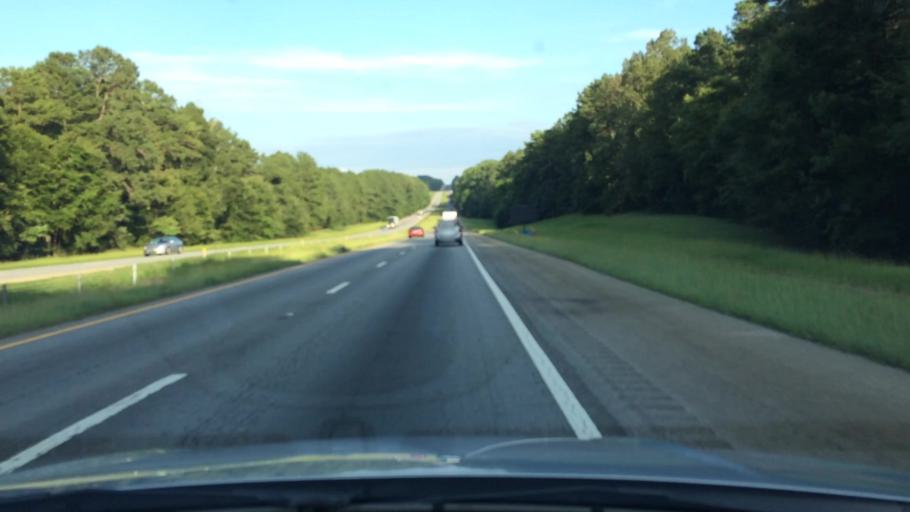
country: US
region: South Carolina
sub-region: Newberry County
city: Newberry
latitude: 34.3593
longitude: -81.6586
